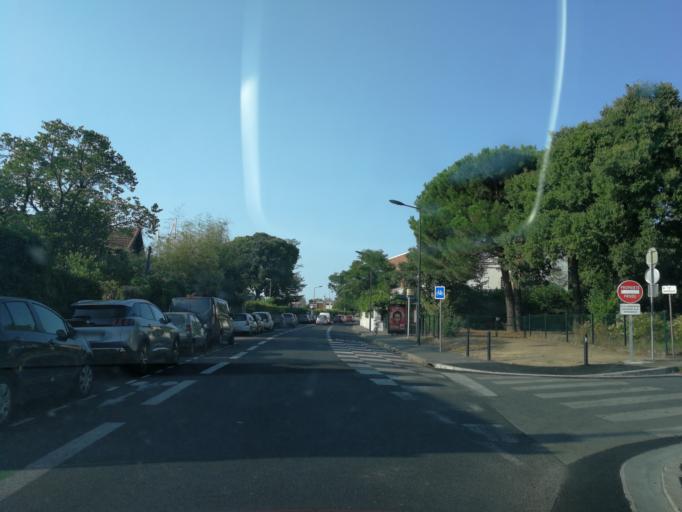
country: FR
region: Midi-Pyrenees
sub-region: Departement de la Haute-Garonne
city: Toulouse
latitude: 43.6237
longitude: 1.4369
